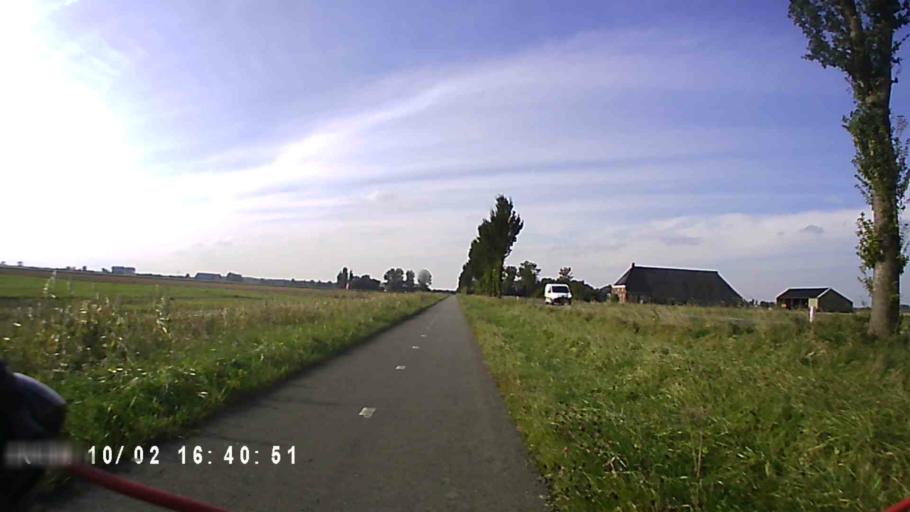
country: NL
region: Groningen
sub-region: Gemeente Zuidhorn
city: Grijpskerk
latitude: 53.3159
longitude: 6.2879
